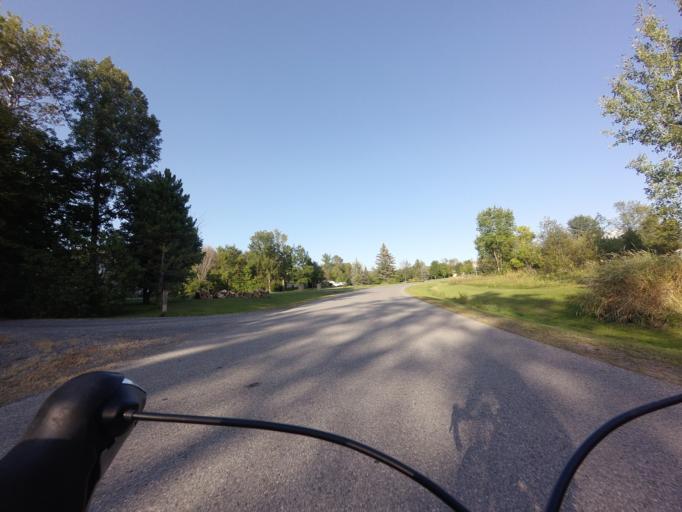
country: CA
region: Ontario
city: Bells Corners
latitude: 45.4443
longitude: -75.9882
